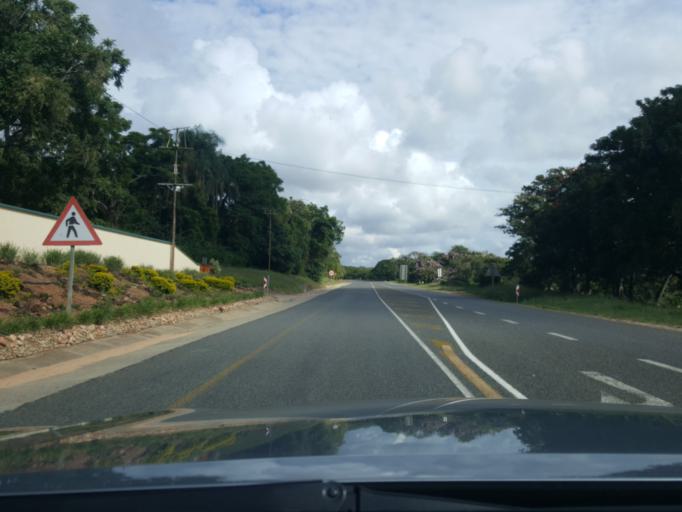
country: ZA
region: Mpumalanga
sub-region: Ehlanzeni District
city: Nelspruit
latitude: -25.4680
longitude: 31.0436
